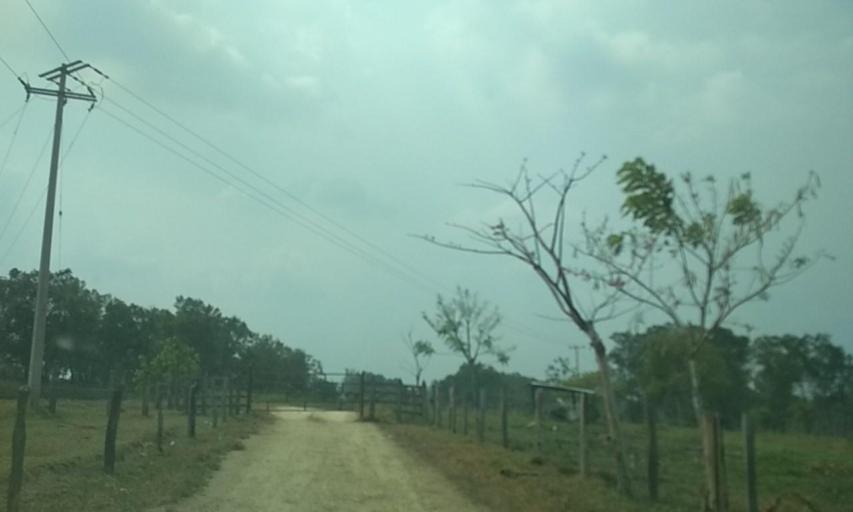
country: MX
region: Veracruz
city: Las Choapas
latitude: 17.8193
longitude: -94.0704
